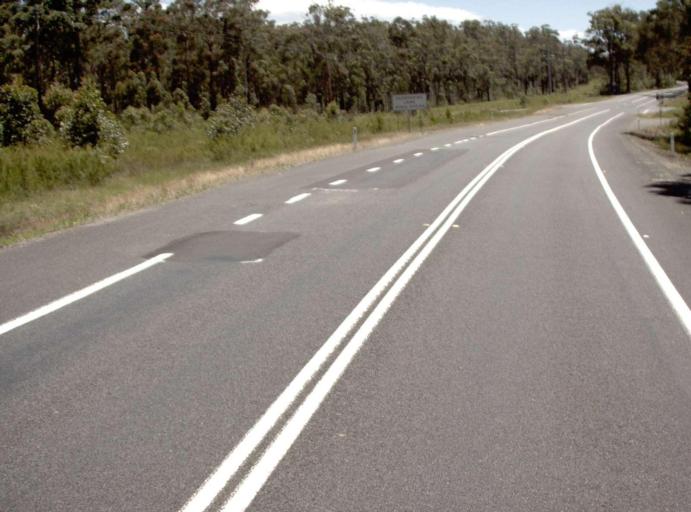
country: AU
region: Victoria
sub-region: East Gippsland
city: Lakes Entrance
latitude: -37.7428
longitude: 148.1587
